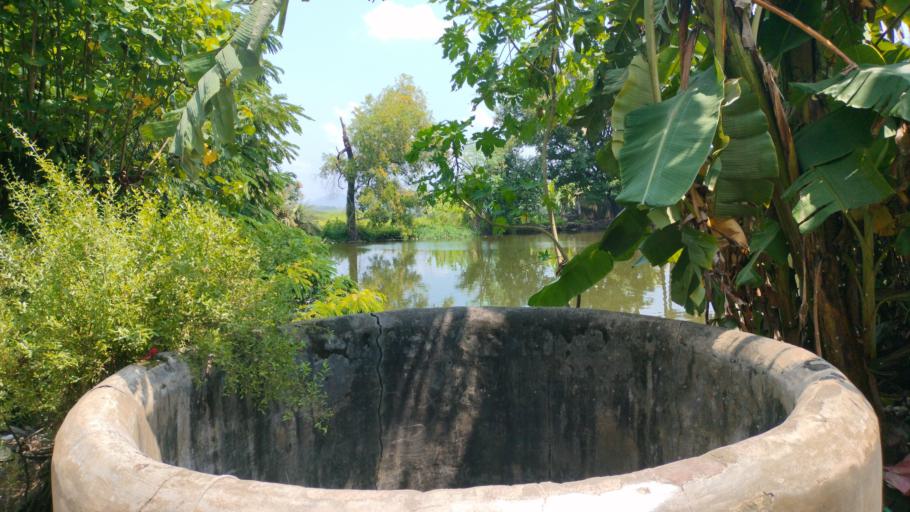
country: IN
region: Maharashtra
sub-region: Thane
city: Bhayandar
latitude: 19.3704
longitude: 72.8016
